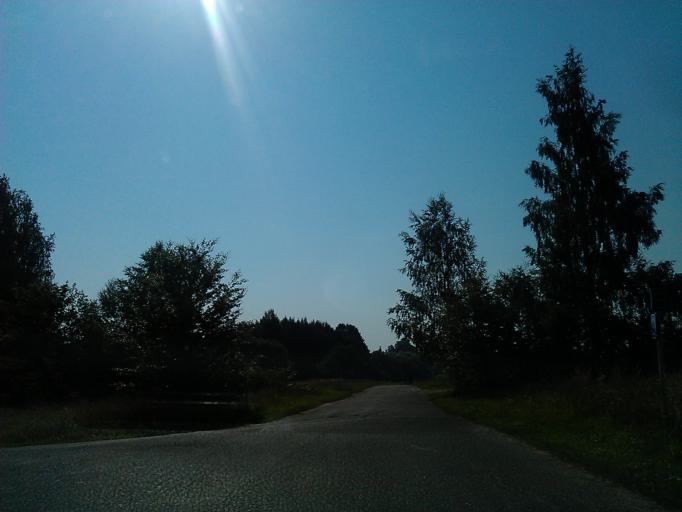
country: LV
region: Aizpute
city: Aizpute
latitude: 56.7128
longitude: 21.6046
